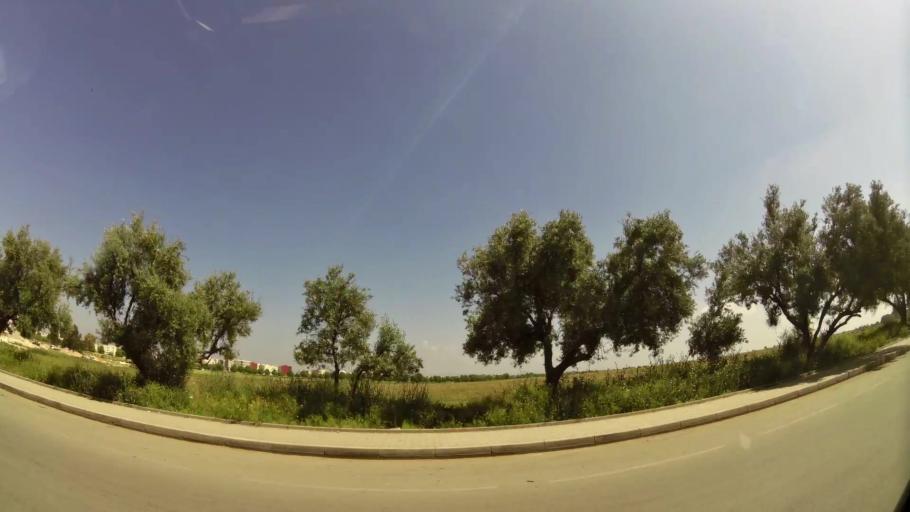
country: MA
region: Fes-Boulemane
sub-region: Fes
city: Fes
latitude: 34.0096
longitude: -5.0254
